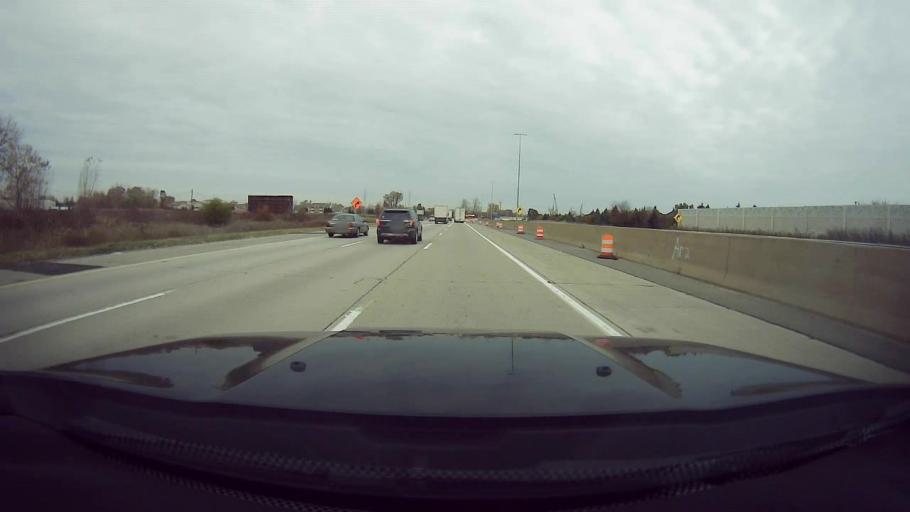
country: US
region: Michigan
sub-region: Wayne County
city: Southgate
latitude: 42.2221
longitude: -83.2145
